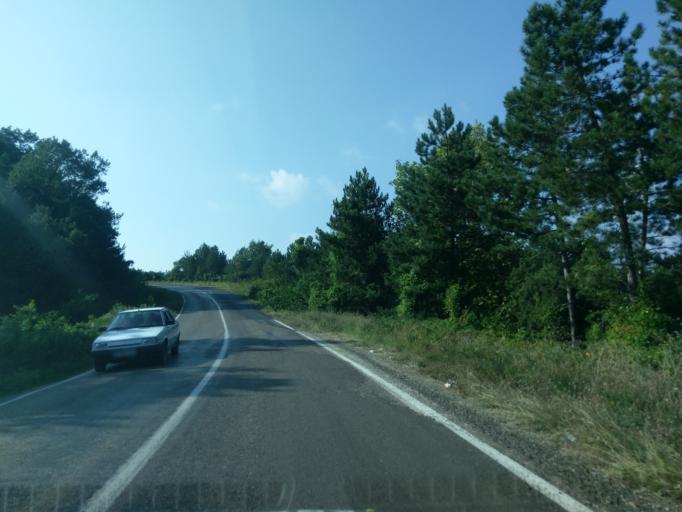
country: TR
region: Sinop
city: Yenikonak
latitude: 41.9422
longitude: 34.7048
